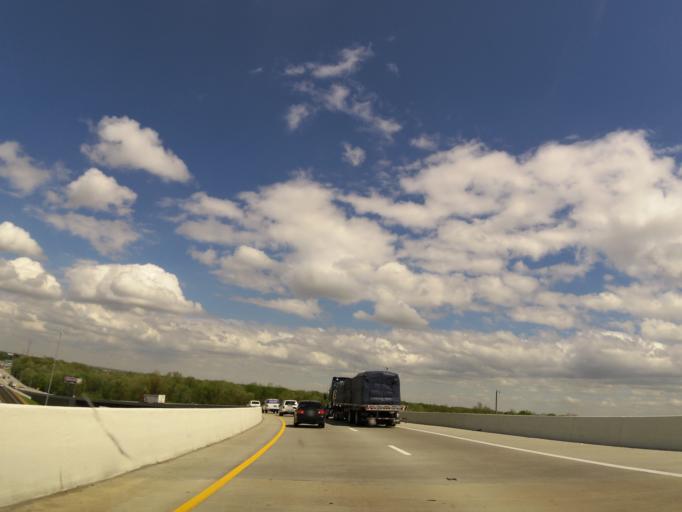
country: US
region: Tennessee
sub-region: Shelby County
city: Bartlett
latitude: 35.1521
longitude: -89.8843
